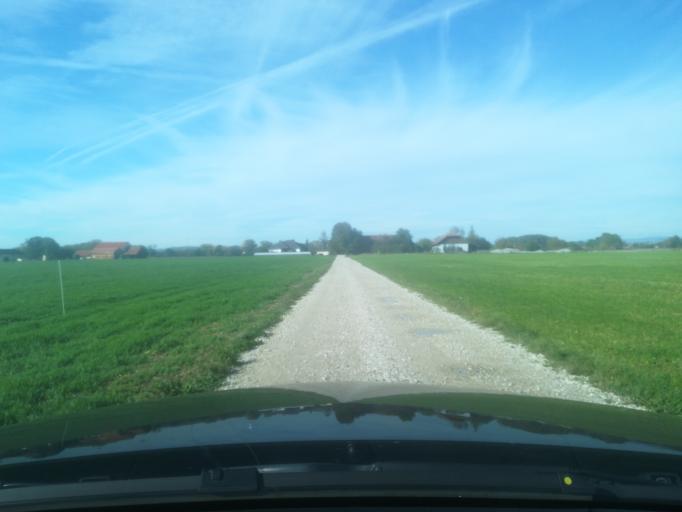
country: AT
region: Upper Austria
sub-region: Politischer Bezirk Linz-Land
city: Horsching
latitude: 48.2053
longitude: 14.1507
